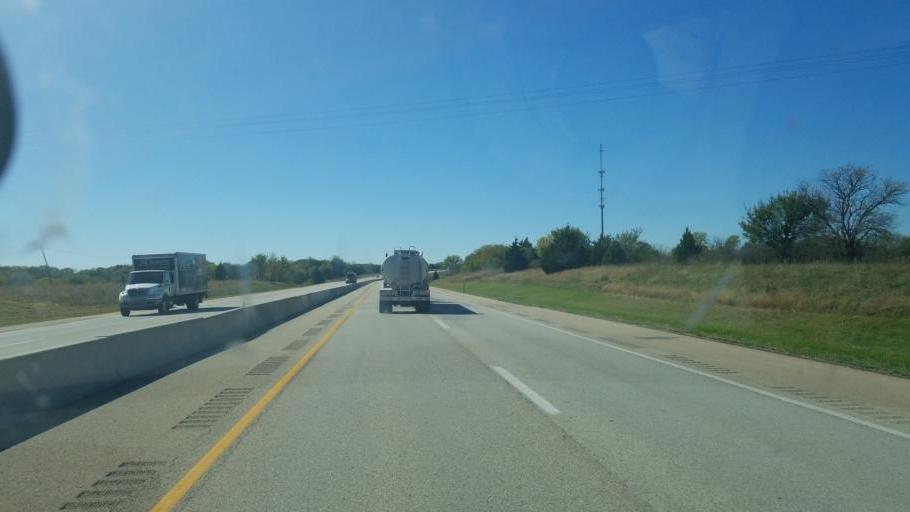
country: US
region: Kansas
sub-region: Douglas County
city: Eudora
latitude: 39.0142
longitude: -95.1455
